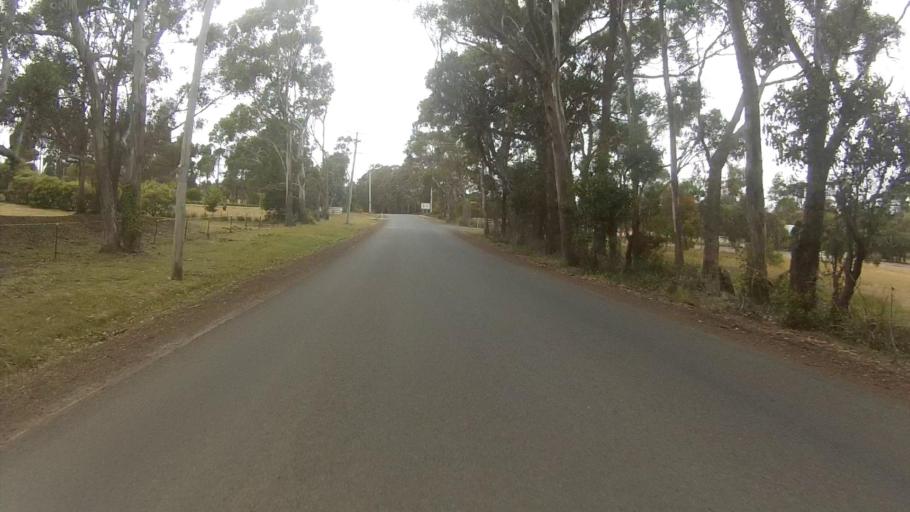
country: AU
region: Tasmania
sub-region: Kingborough
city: Kingston
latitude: -42.9656
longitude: 147.2385
